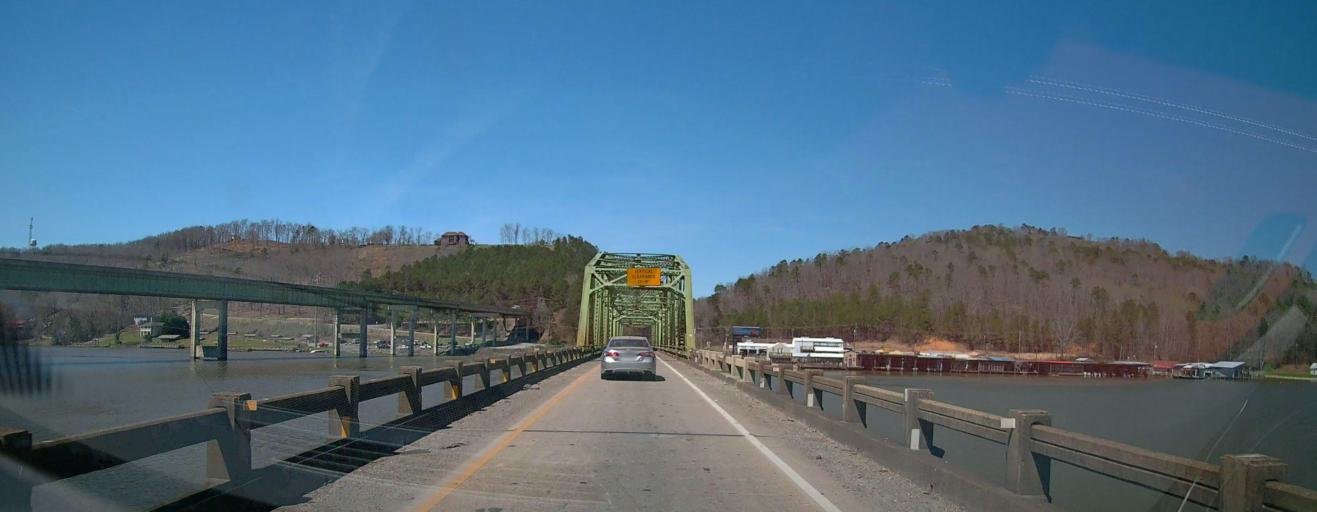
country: US
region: Alabama
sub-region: Etowah County
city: Southside
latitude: 33.9420
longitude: -86.0250
